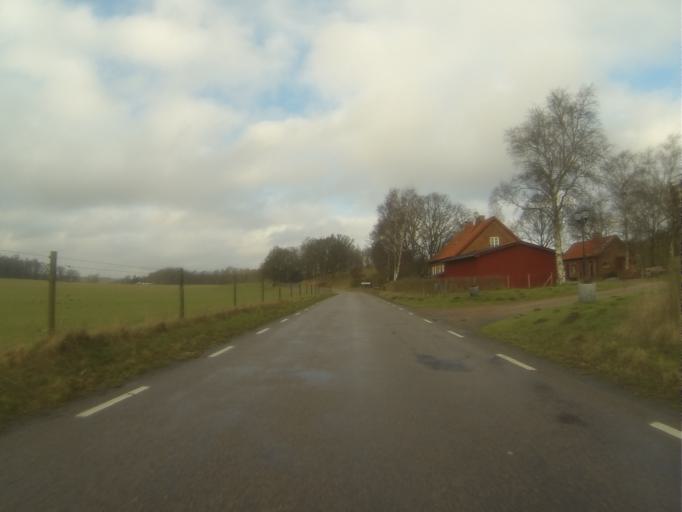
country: SE
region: Skane
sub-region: Lunds Kommun
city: Genarp
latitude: 55.5611
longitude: 13.3164
